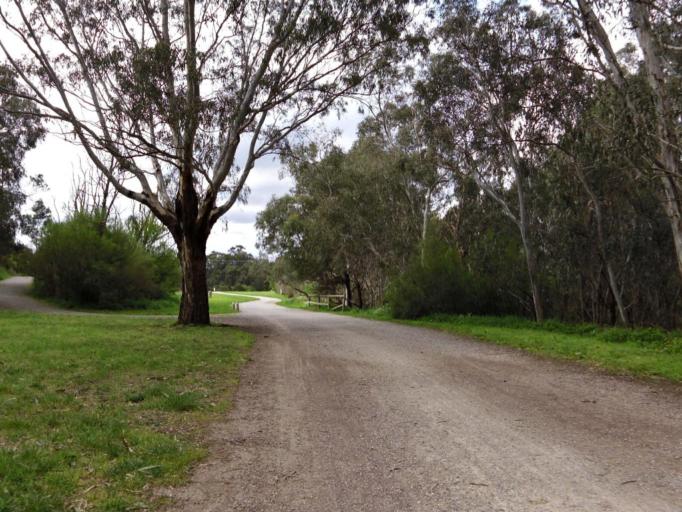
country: AU
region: Victoria
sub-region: Manningham
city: Bulleen
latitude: -37.7713
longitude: 145.0703
